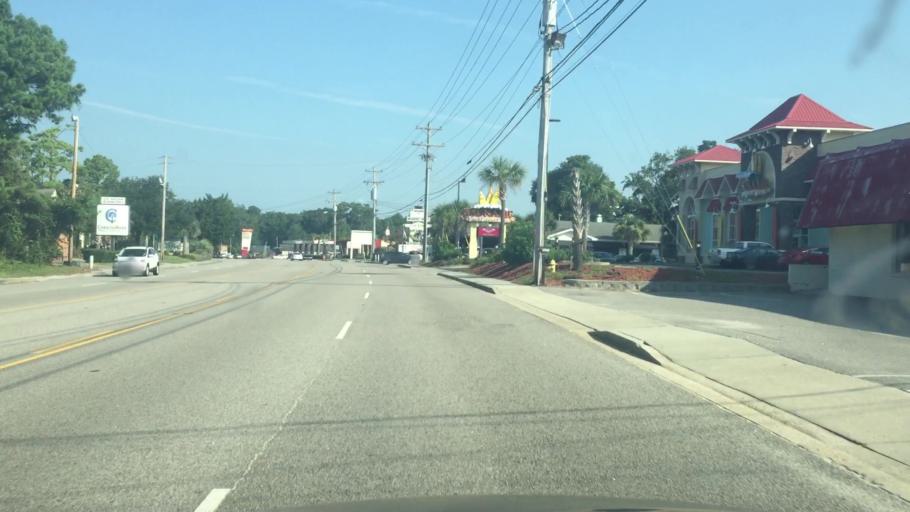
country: US
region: South Carolina
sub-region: Horry County
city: North Myrtle Beach
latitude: 33.8397
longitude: -78.6453
